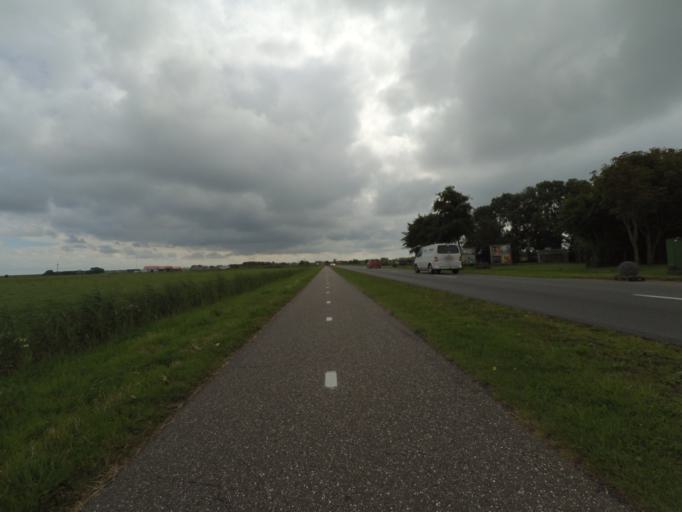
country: NL
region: North Holland
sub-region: Gemeente Texel
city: Den Burg
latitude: 53.0431
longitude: 4.8352
